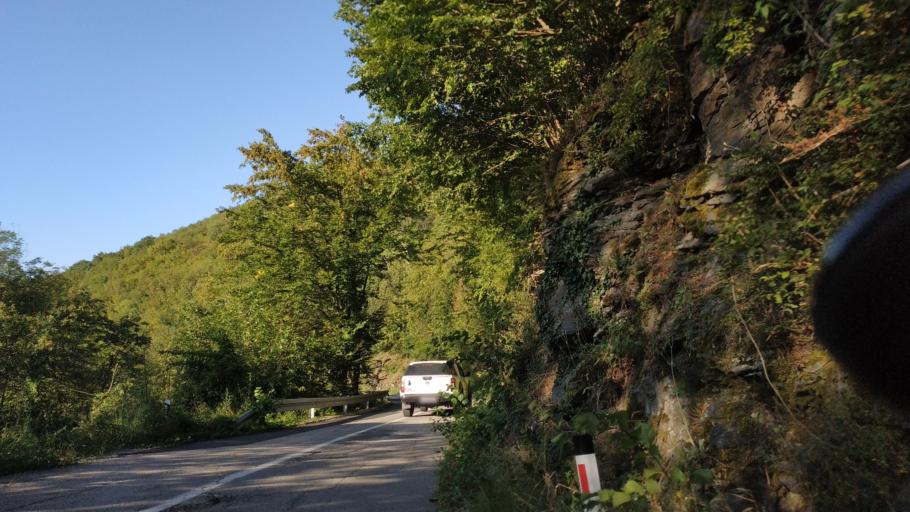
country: RS
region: Central Serbia
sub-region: Rasinski Okrug
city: Krusevac
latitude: 43.4640
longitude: 21.3597
